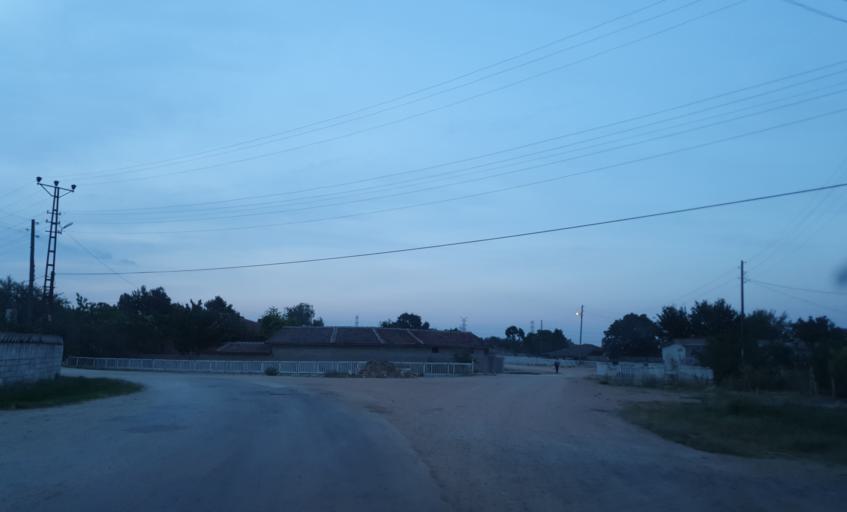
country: TR
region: Kirklareli
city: Vize
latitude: 41.4850
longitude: 27.7531
